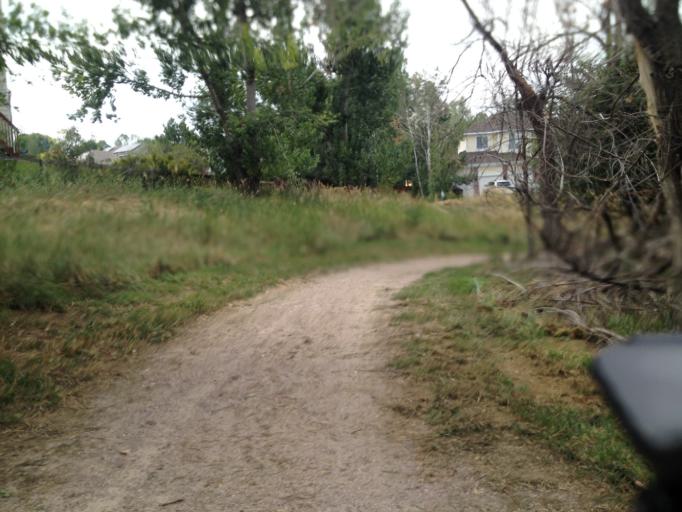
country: US
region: Colorado
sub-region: Boulder County
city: Louisville
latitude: 39.9861
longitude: -105.1482
